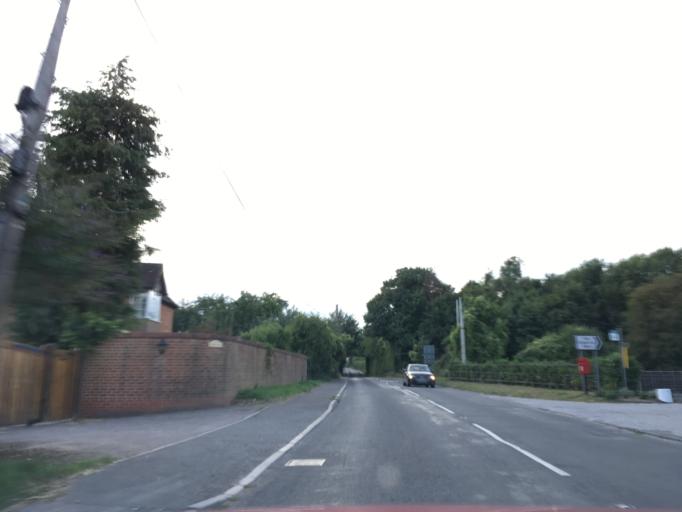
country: GB
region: England
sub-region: Wiltshire
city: Market Lavington
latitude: 51.3308
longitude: -1.9404
